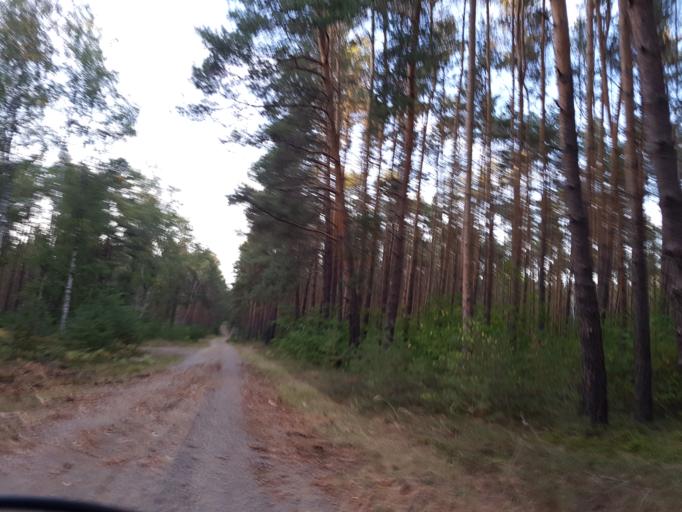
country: DE
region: Brandenburg
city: Schonborn
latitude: 51.5691
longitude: 13.4628
